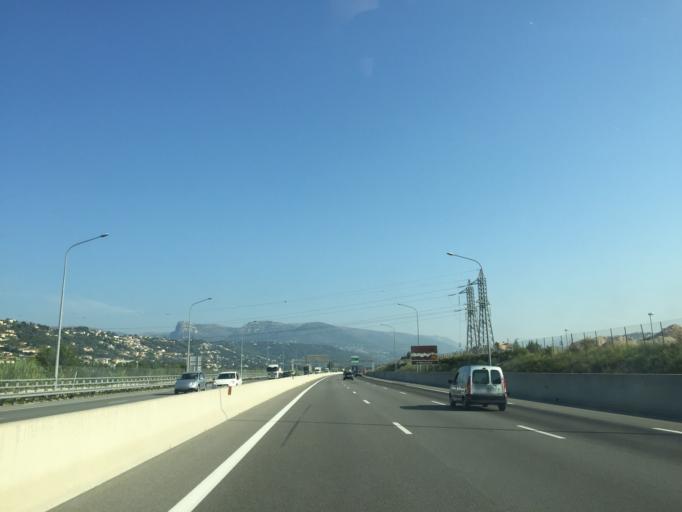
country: FR
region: Provence-Alpes-Cote d'Azur
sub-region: Departement des Alpes-Maritimes
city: Saint-Laurent-du-Var
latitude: 43.6836
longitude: 7.1921
